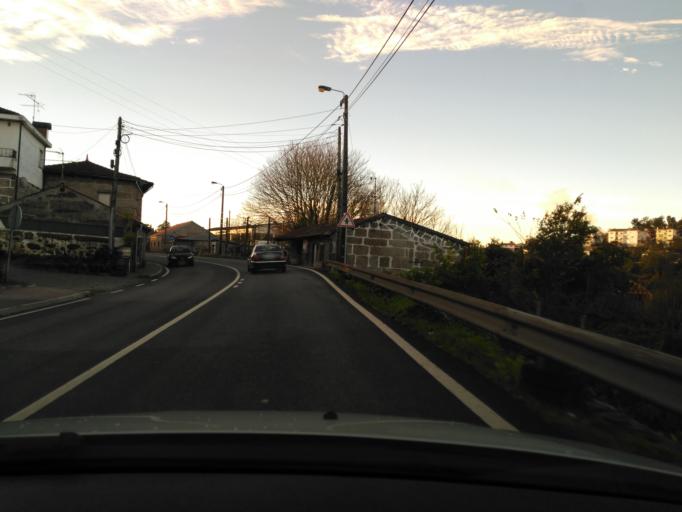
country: PT
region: Braga
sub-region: Guimaraes
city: Guimaraes
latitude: 41.4534
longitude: -8.3099
